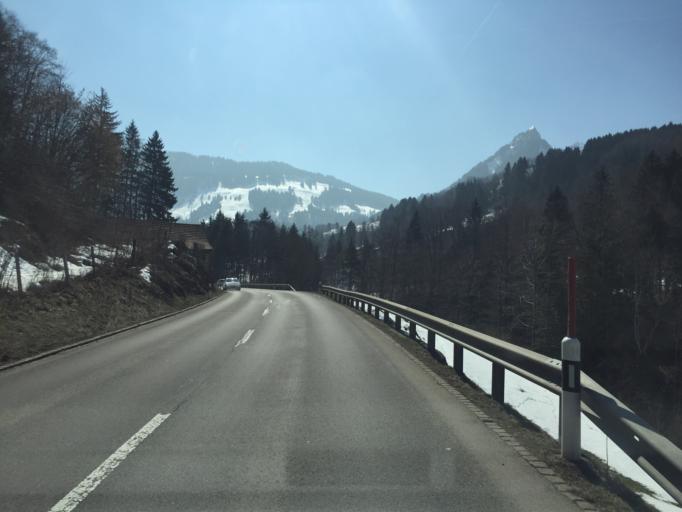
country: CH
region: Saint Gallen
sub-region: Wahlkreis Toggenburg
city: Krummenau
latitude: 47.2099
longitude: 9.2175
